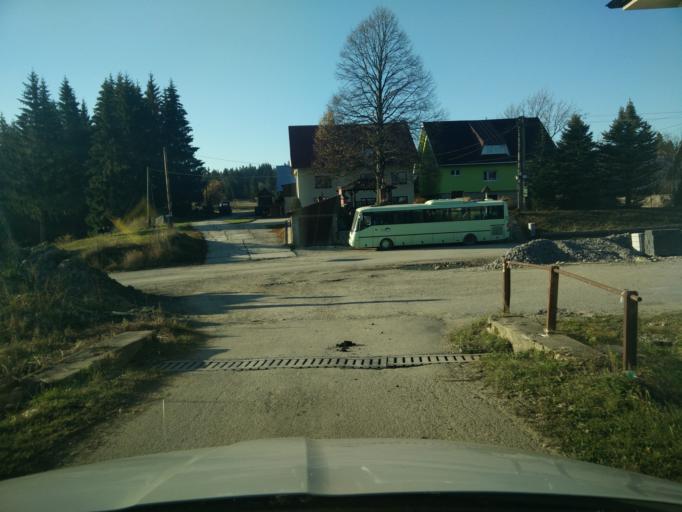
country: SK
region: Zilinsky
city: Oravska Lesna
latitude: 49.3592
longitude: 19.1495
